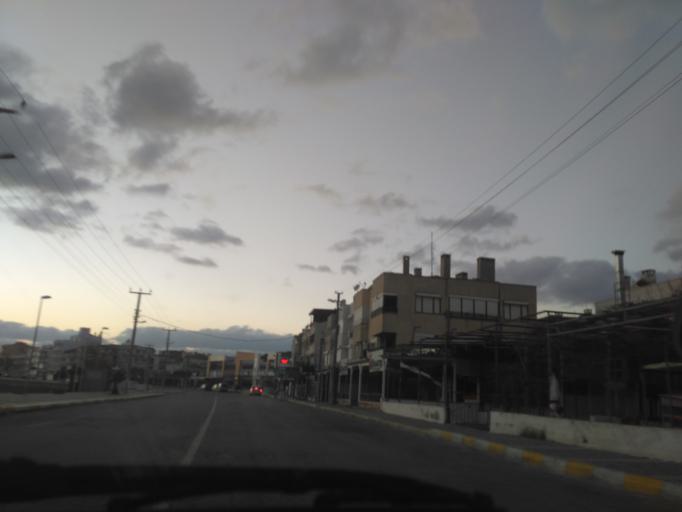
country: TR
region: Balikesir
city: Ayvalik
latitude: 39.2693
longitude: 26.6655
